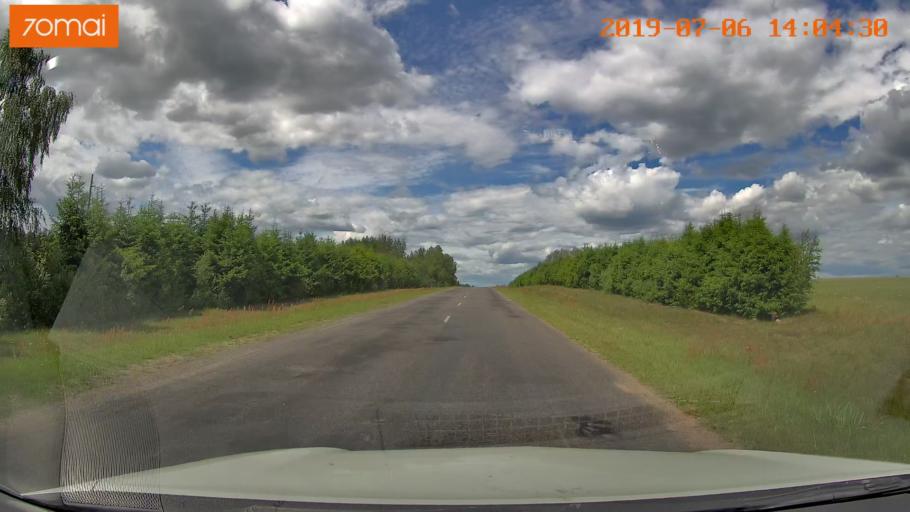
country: BY
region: Minsk
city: Ivyanyets
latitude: 53.8404
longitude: 26.7988
